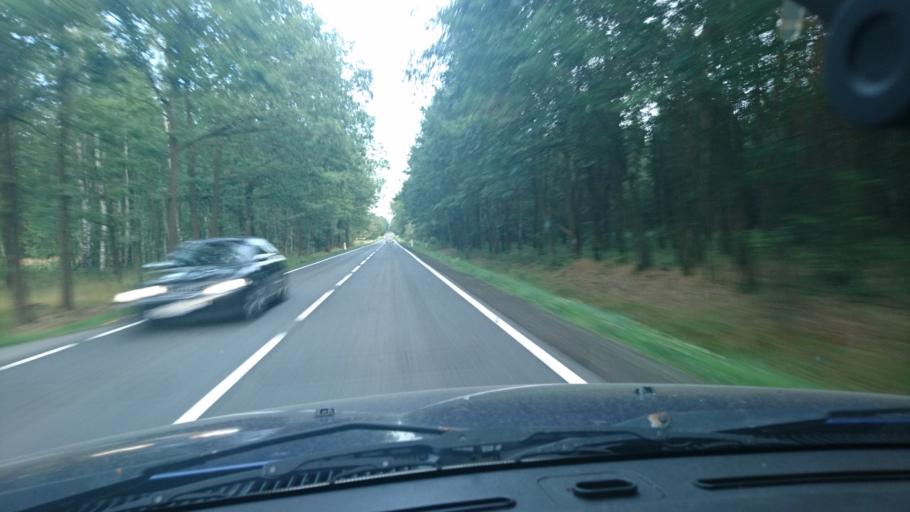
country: PL
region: Opole Voivodeship
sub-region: Powiat oleski
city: Olesno
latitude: 50.8488
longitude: 18.4745
